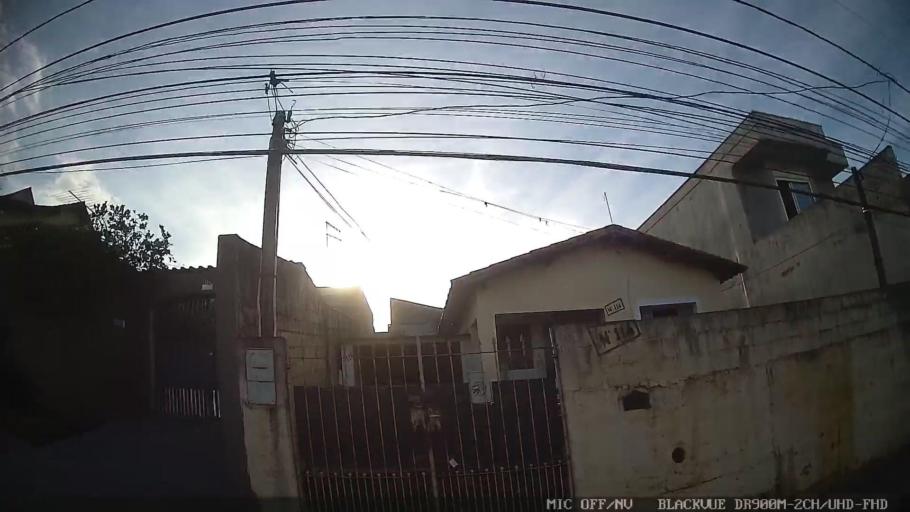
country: BR
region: Sao Paulo
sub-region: Mogi das Cruzes
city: Mogi das Cruzes
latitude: -23.5121
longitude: -46.1435
